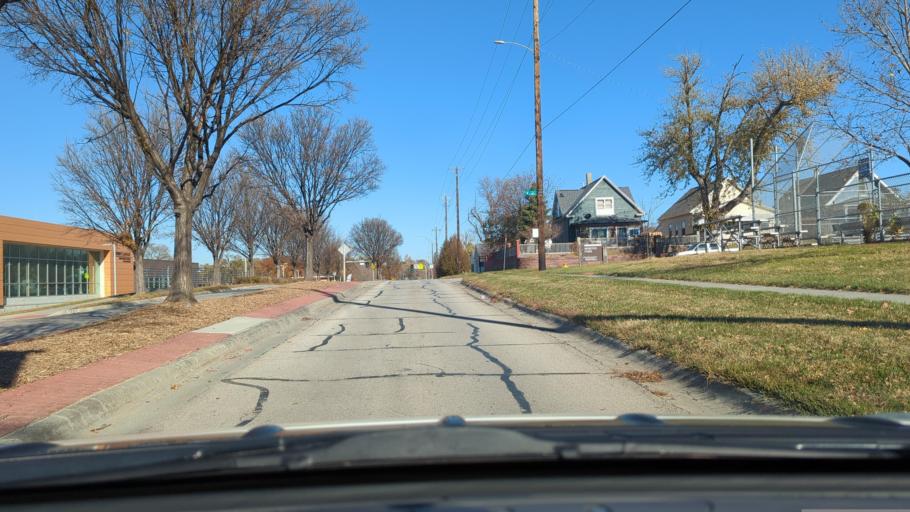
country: US
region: Nebraska
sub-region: Sarpy County
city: La Vista
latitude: 41.2004
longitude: -95.9770
